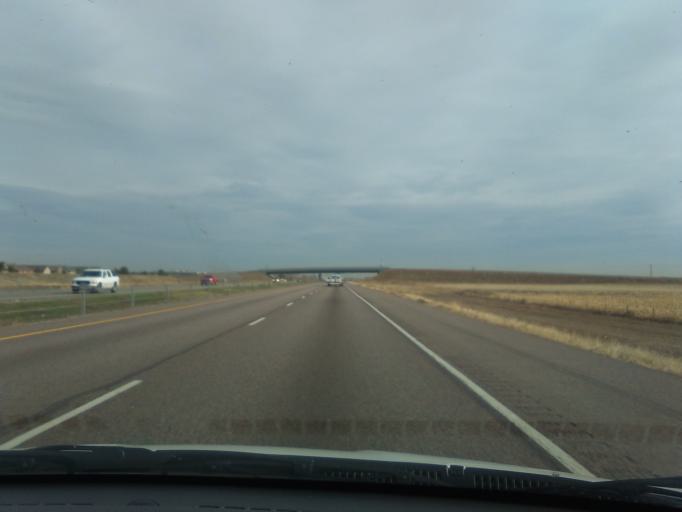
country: US
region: Colorado
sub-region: Adams County
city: Todd Creek
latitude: 39.8949
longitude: -104.8505
